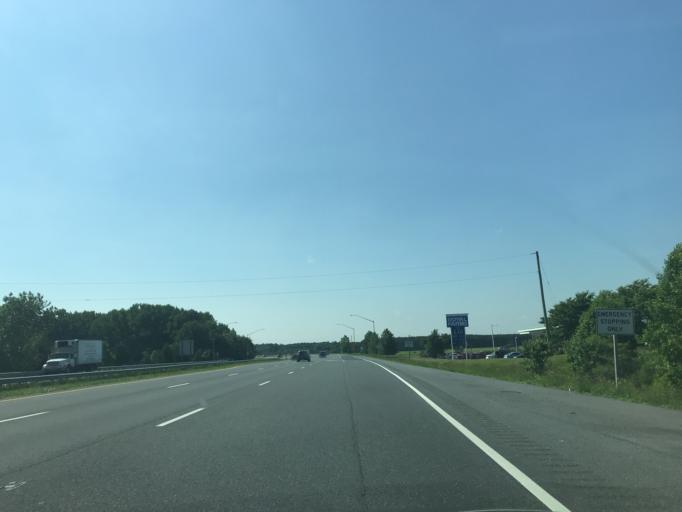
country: US
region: Maryland
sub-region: Wicomico County
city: Hebron
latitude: 38.4086
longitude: -75.6412
